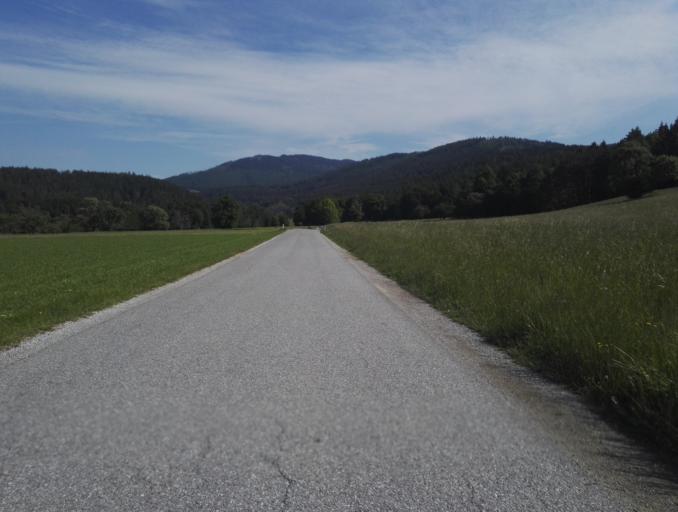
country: AT
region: Styria
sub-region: Politischer Bezirk Graz-Umgebung
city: Stattegg
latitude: 47.1460
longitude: 15.4339
